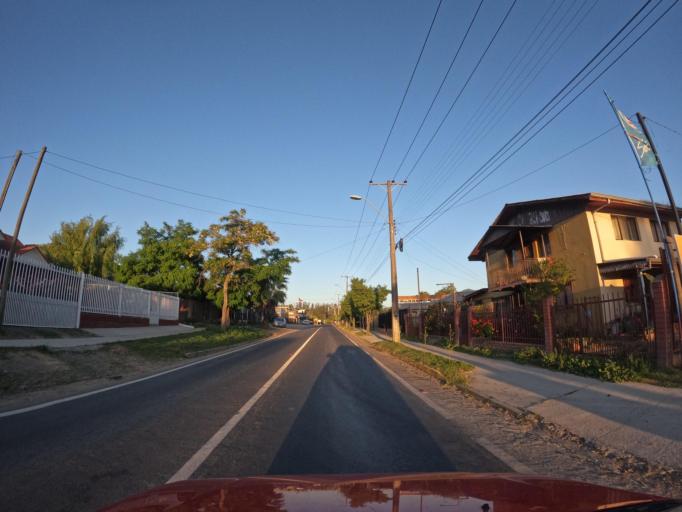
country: CL
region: Maule
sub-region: Provincia de Talca
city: Talca
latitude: -35.0900
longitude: -71.6540
